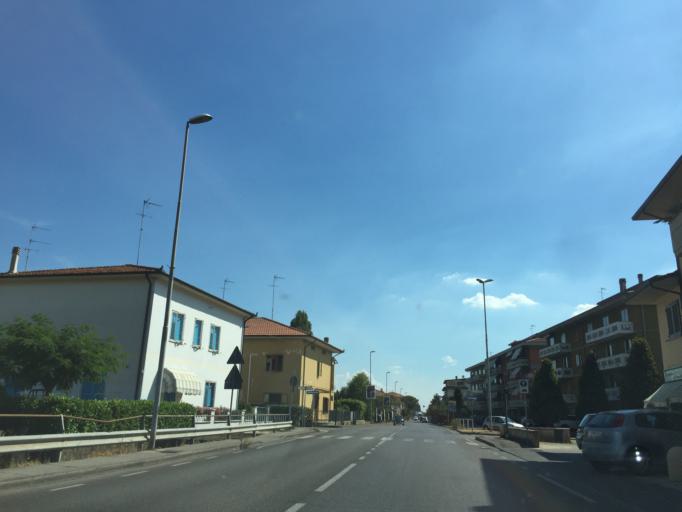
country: IT
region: Tuscany
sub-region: Provincia di Pistoia
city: Monsummano Terme
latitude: 43.8749
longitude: 10.8116
